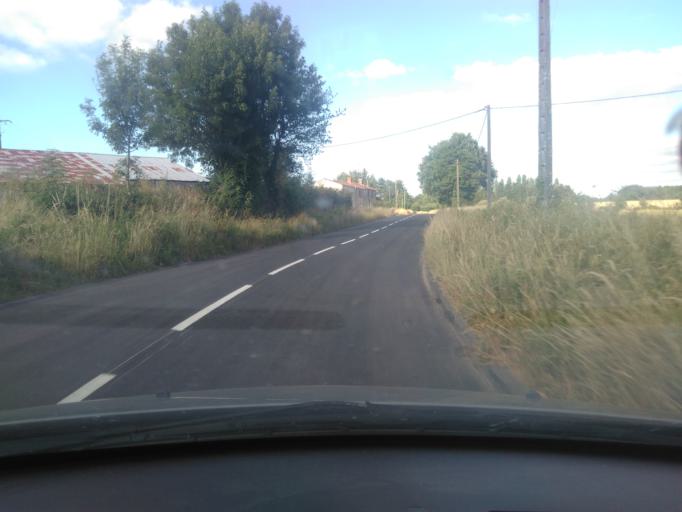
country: FR
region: Pays de la Loire
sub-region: Departement de la Vendee
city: Saint-Florent-des-Bois
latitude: 46.5776
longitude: -1.3296
